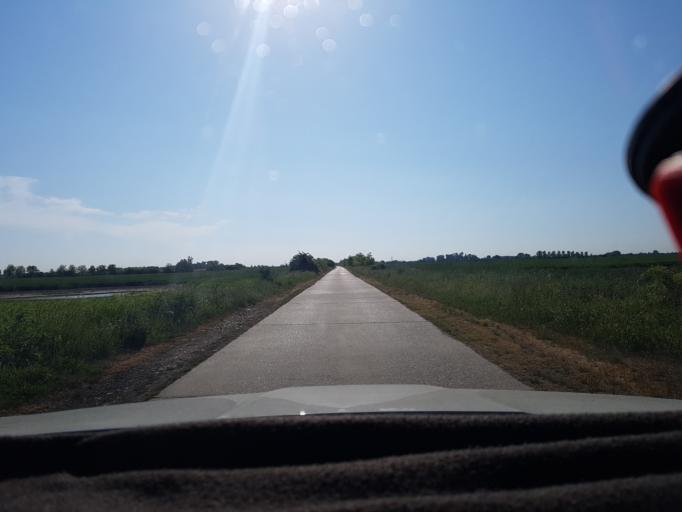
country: HU
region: Tolna
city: Decs
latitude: 46.2771
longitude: 18.7104
